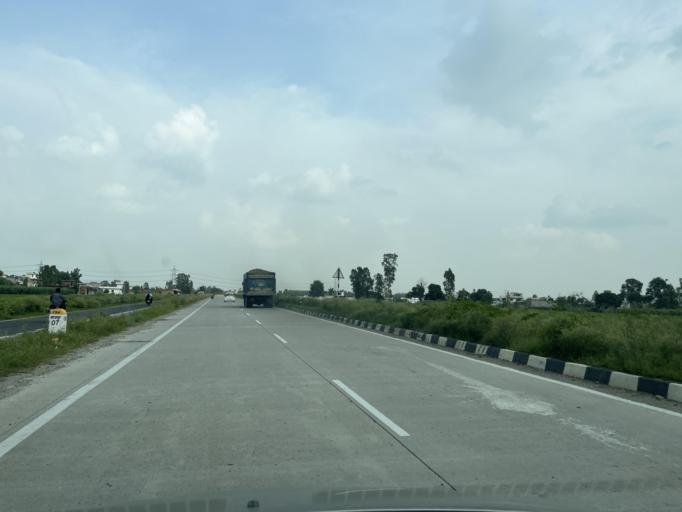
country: IN
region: Uttarakhand
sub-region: Udham Singh Nagar
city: Bazpur
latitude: 29.1504
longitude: 79.0733
